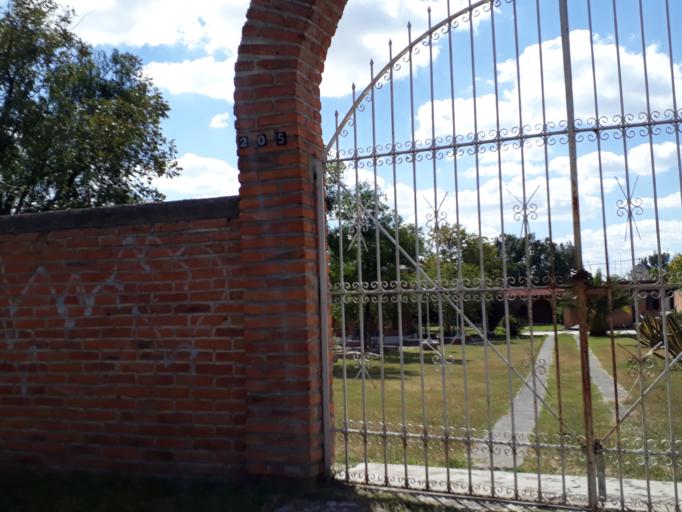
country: MX
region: Aguascalientes
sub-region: Aguascalientes
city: San Sebastian [Fraccionamiento]
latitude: 21.7899
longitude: -102.2797
